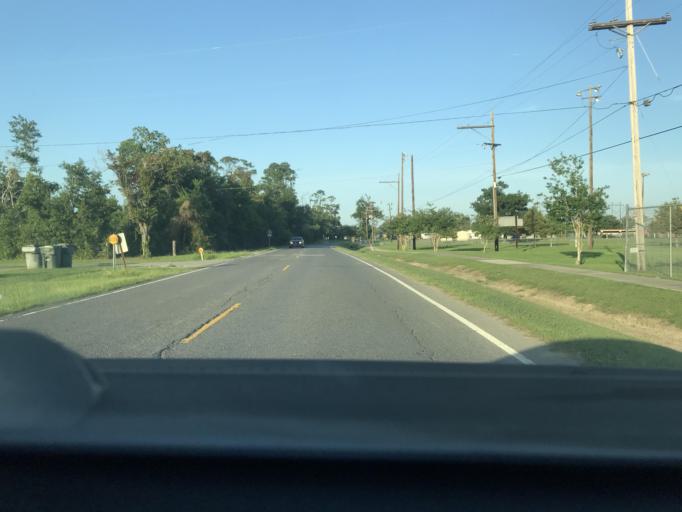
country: US
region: Louisiana
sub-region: Calcasieu Parish
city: Moss Bluff
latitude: 30.2639
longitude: -93.1894
